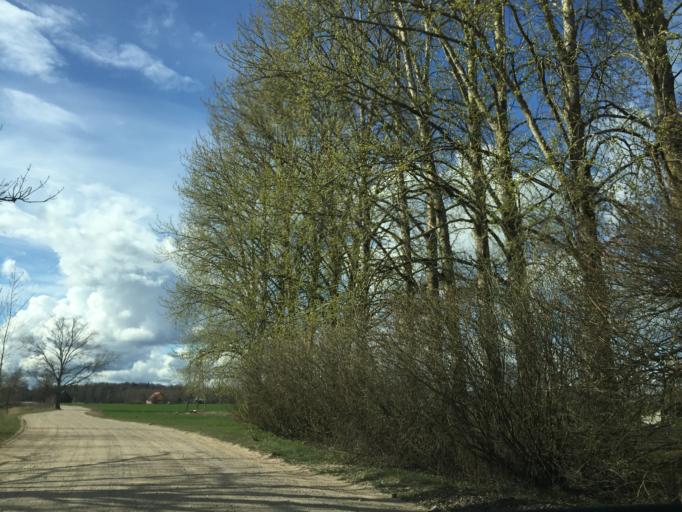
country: LV
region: Burtnieki
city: Matisi
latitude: 57.5976
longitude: 25.0722
